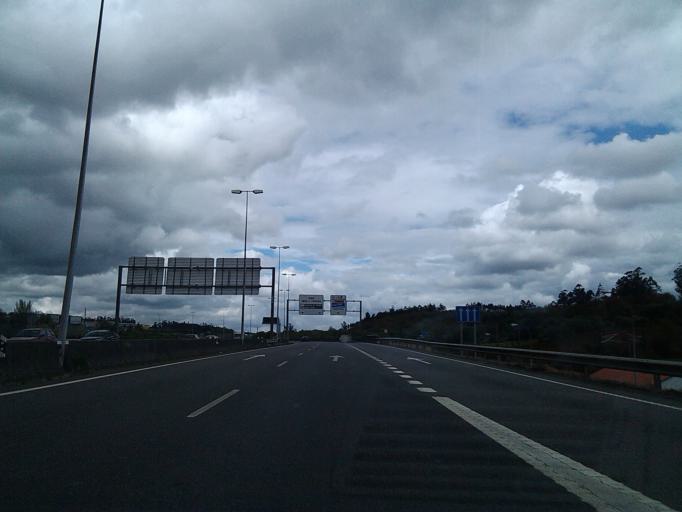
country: ES
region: Galicia
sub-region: Provincia da Coruna
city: Santiago de Compostela
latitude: 42.8917
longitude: -8.5076
